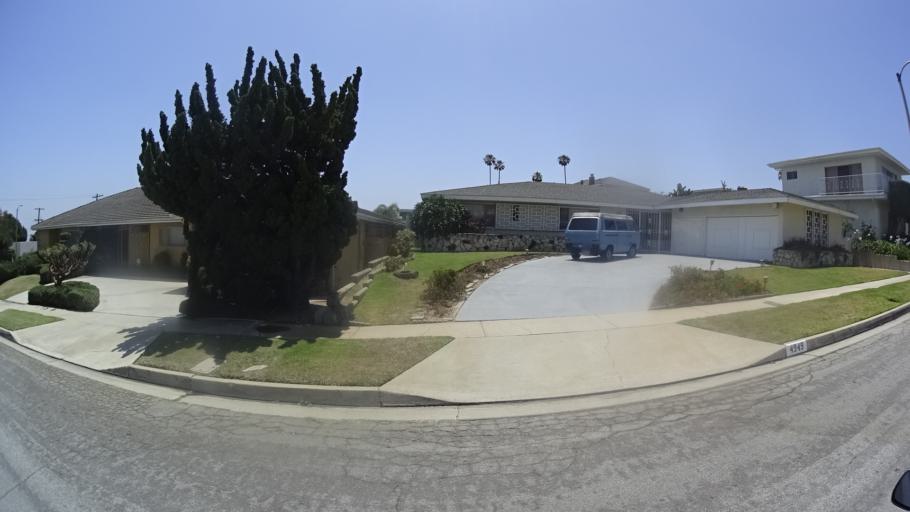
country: US
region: California
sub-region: Los Angeles County
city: View Park-Windsor Hills
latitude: 33.9978
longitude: -118.3519
